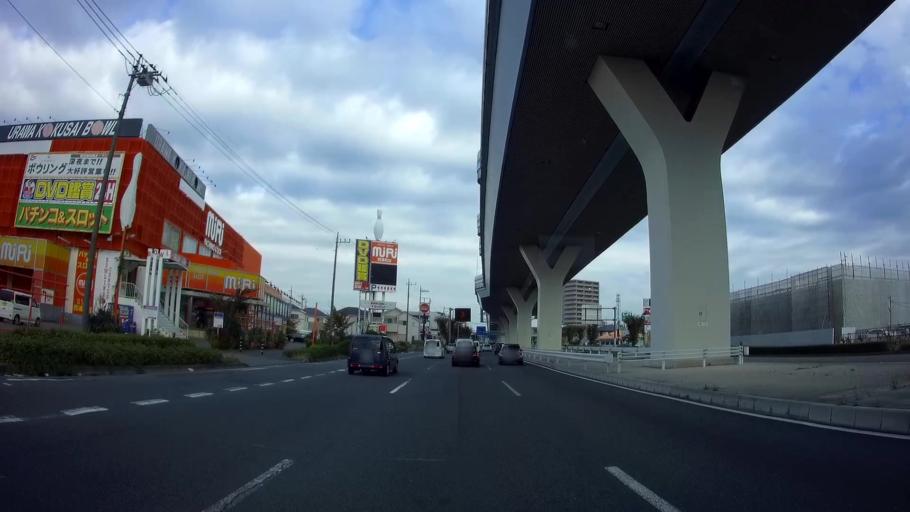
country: JP
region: Saitama
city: Yono
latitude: 35.8616
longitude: 139.6210
